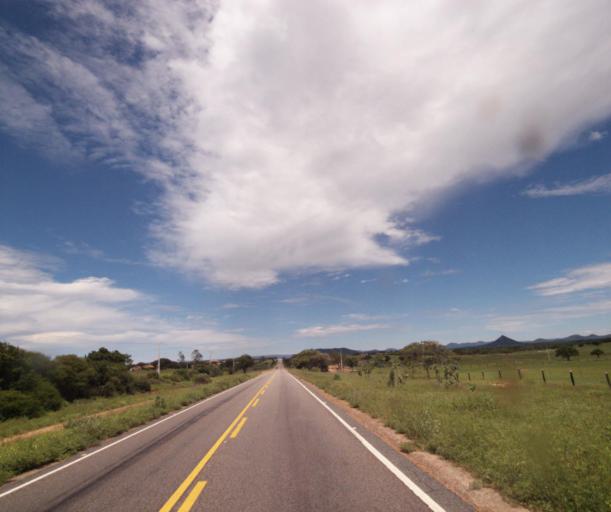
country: BR
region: Bahia
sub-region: Guanambi
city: Guanambi
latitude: -14.2320
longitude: -42.9488
